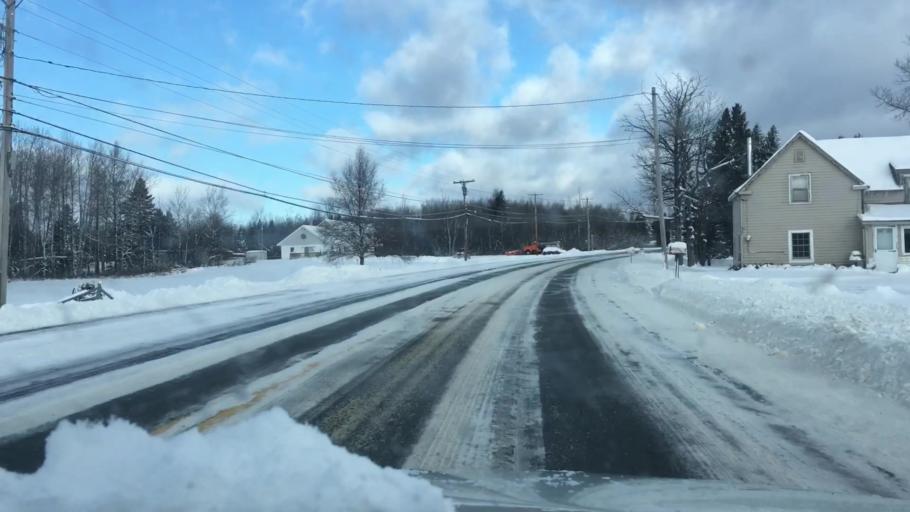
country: US
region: Maine
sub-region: Aroostook County
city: Caribou
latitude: 46.9295
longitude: -68.0229
